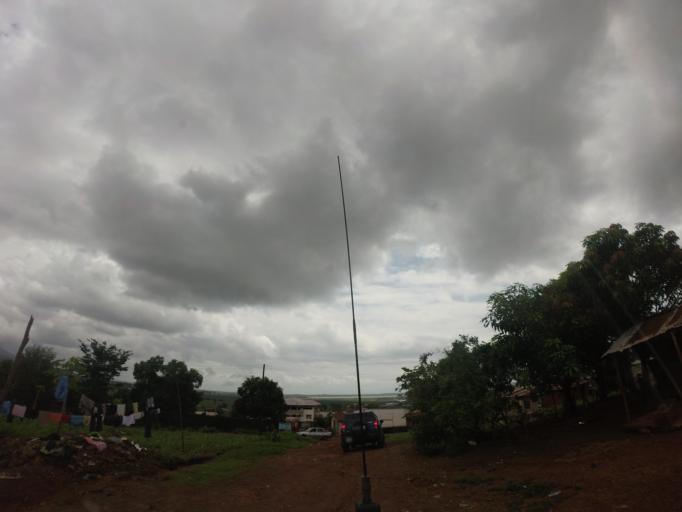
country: SL
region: Western Area
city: Hastings
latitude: 8.3880
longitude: -13.1242
